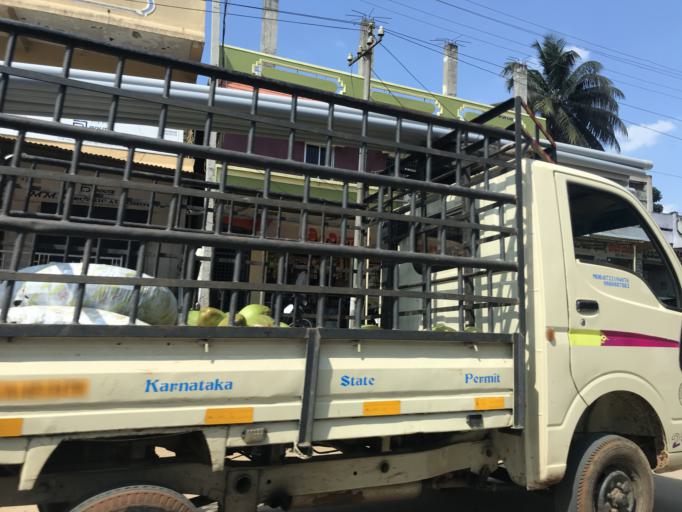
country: IN
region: Karnataka
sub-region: Mysore
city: Heggadadevankote
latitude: 12.0893
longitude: 76.3318
